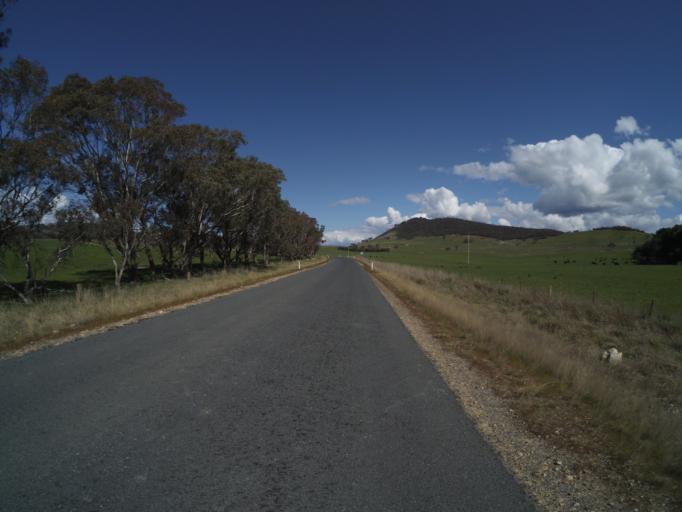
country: AU
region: New South Wales
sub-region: Yass Valley
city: Murrumbateman
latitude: -35.1329
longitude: 148.8709
